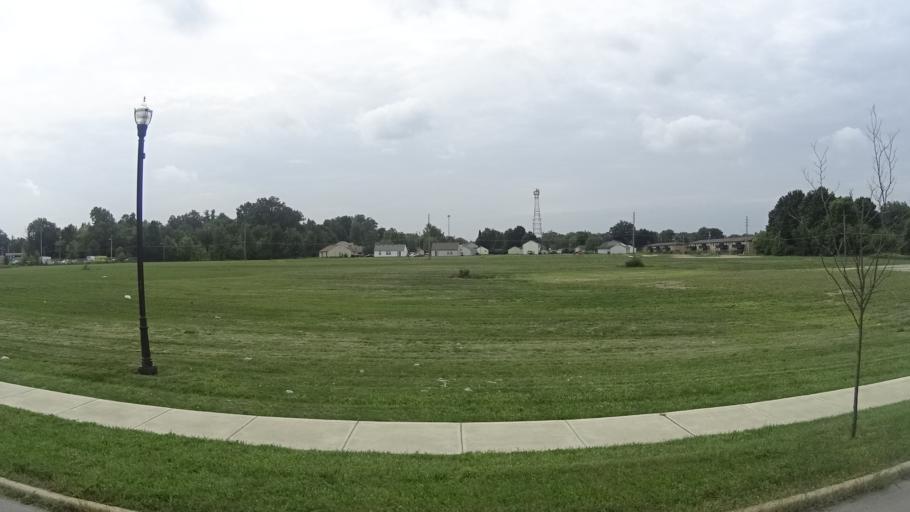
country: US
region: Indiana
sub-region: Madison County
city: Edgewood
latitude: 40.1017
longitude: -85.7148
